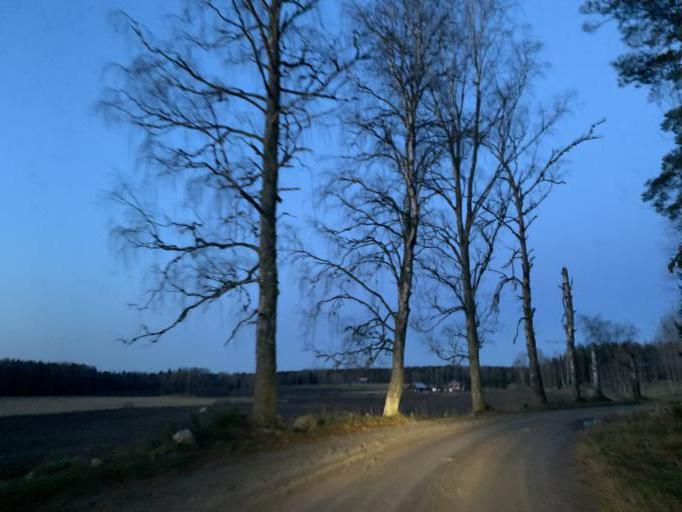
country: SE
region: OErebro
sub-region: Lindesbergs Kommun
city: Fellingsbro
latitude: 59.3607
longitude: 15.5897
